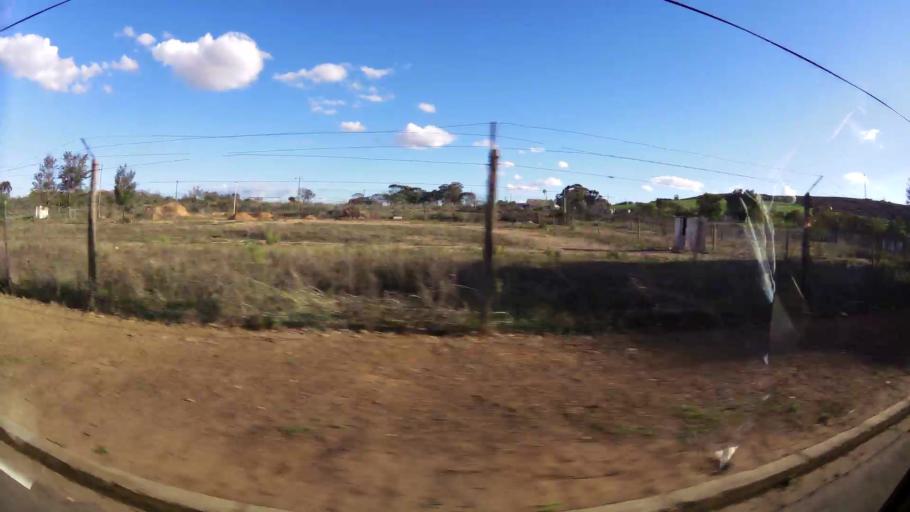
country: ZA
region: Western Cape
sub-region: Eden District Municipality
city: Riversdale
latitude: -34.0985
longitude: 20.9572
